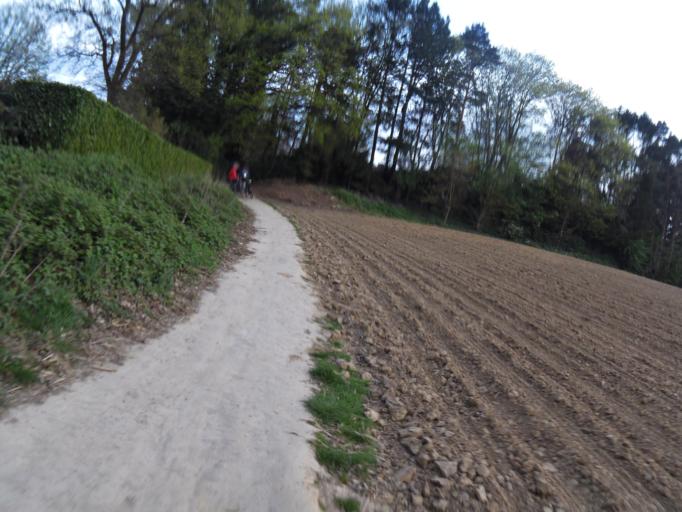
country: BE
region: Flanders
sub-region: Provincie Vlaams-Brabant
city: Wezembeek-Oppem
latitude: 50.8258
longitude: 4.4677
